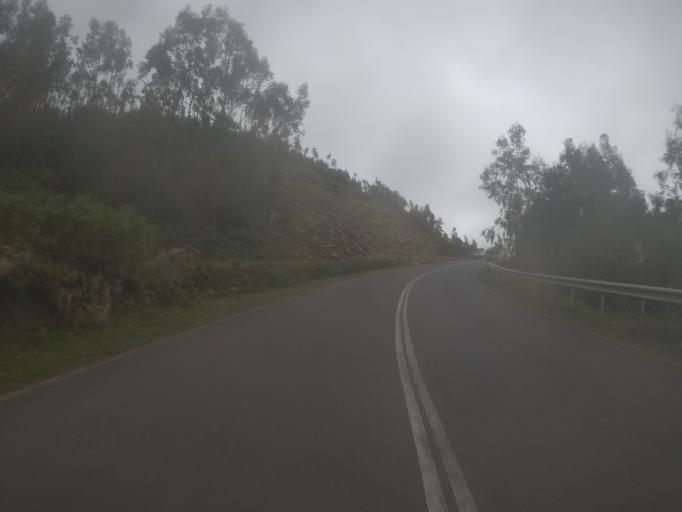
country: ET
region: Amhara
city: Gondar
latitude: 12.7490
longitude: 37.5289
